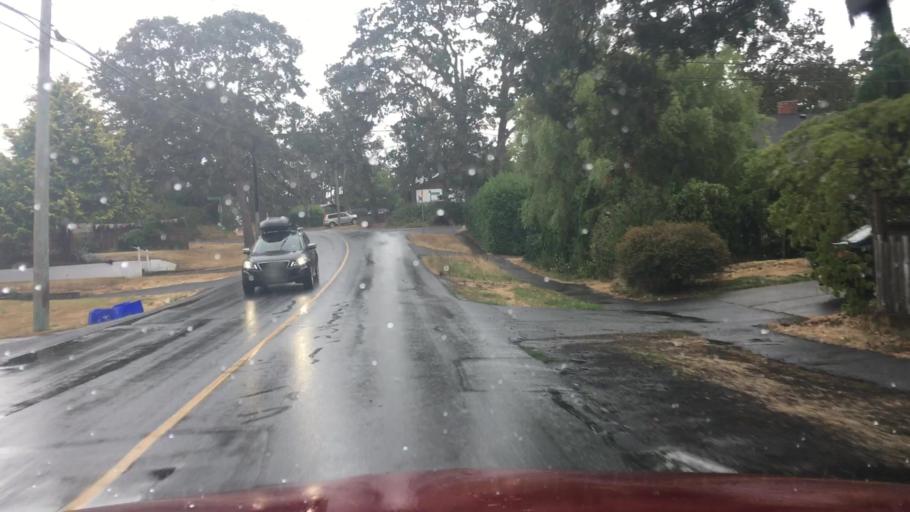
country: CA
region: British Columbia
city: Victoria
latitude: 48.4551
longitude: -123.3509
